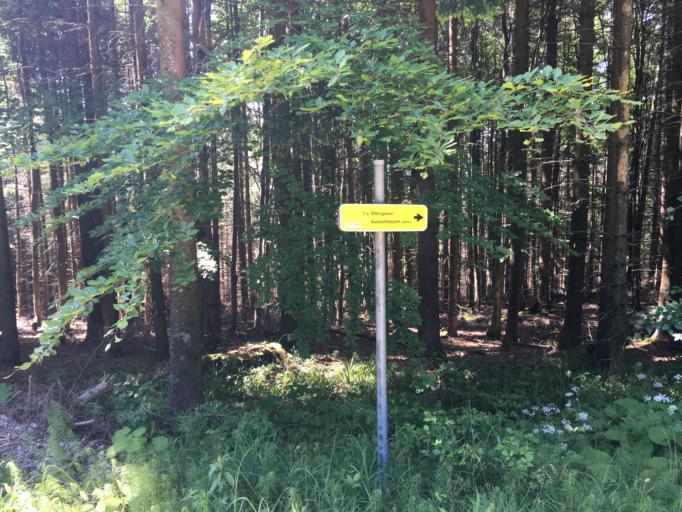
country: AT
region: Upper Austria
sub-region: Politischer Bezirk Vocklabruck
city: Sankt Georgen im Attergau
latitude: 47.9338
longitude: 13.4327
